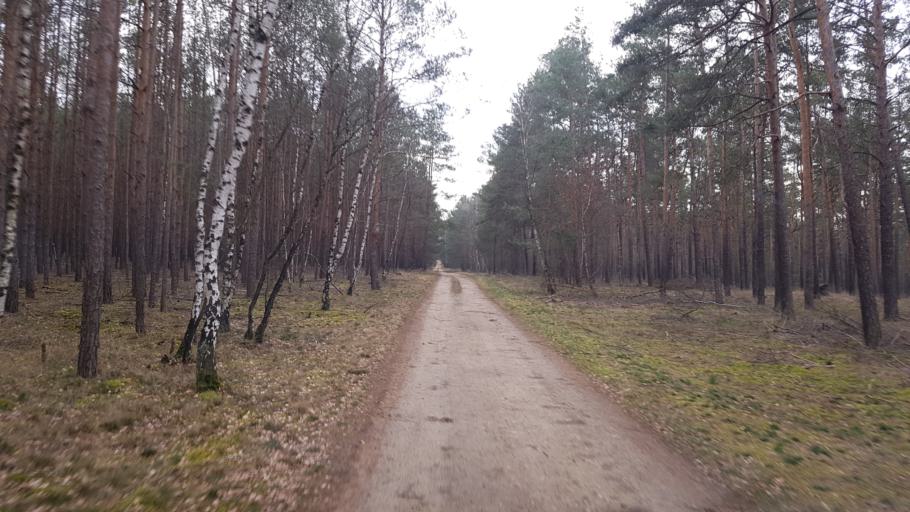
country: DE
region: Brandenburg
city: Schilda
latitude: 51.6279
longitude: 13.3820
